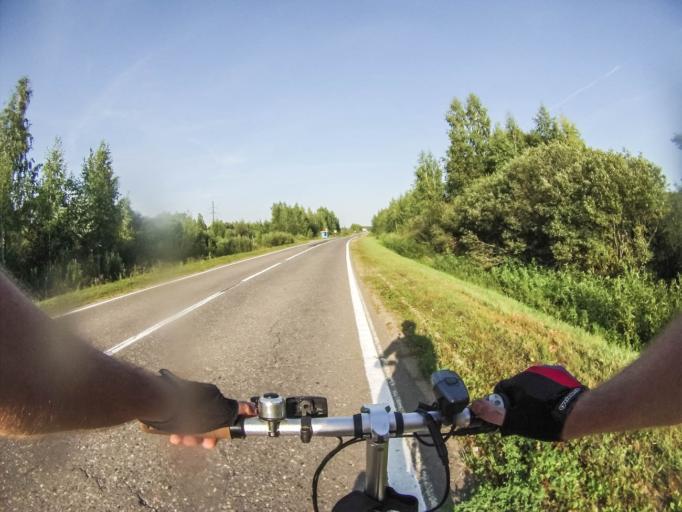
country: RU
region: Jaroslavl
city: Myshkin
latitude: 57.7099
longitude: 38.3705
